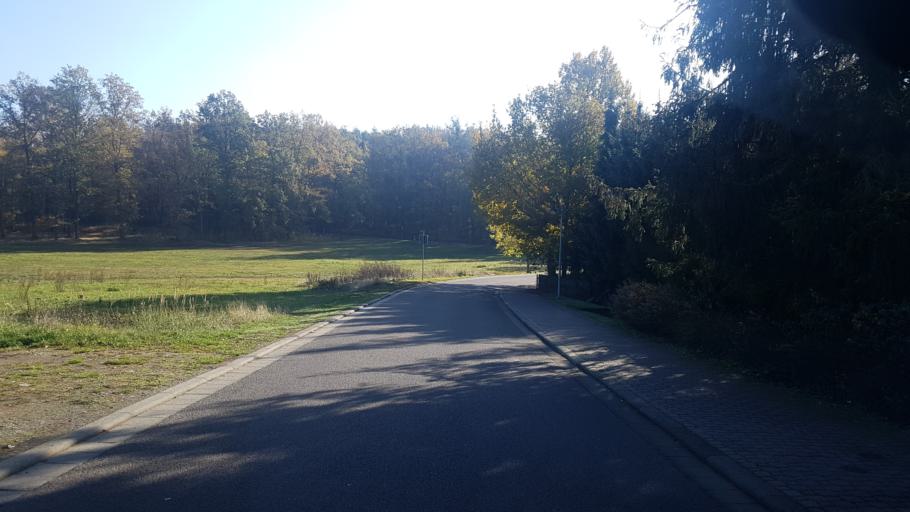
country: DE
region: Saxony
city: Dahlen
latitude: 51.3970
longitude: 12.9977
